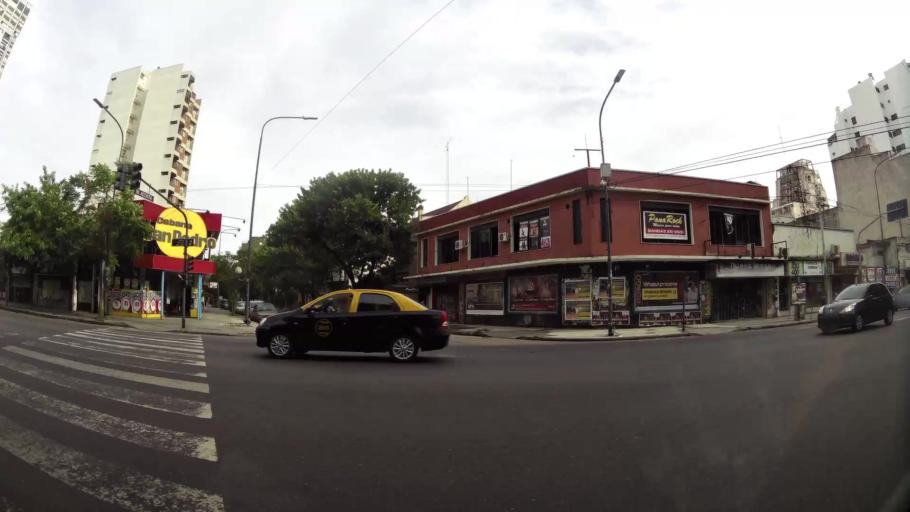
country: AR
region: Buenos Aires F.D.
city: Villa Santa Rita
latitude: -34.6337
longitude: -58.4823
